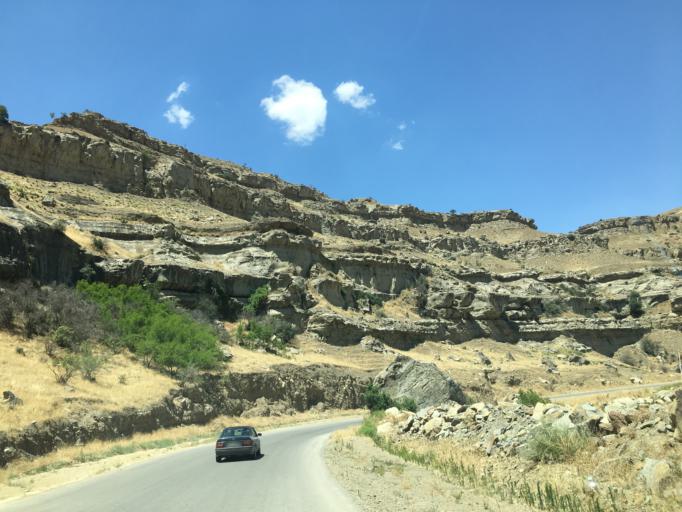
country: TM
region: Balkan
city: Magtymguly
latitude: 38.4240
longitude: 56.6415
